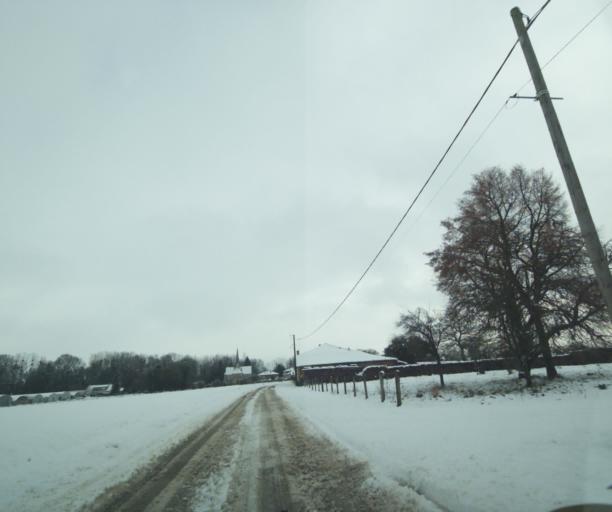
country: FR
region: Champagne-Ardenne
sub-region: Departement de la Haute-Marne
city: Montier-en-Der
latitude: 48.4967
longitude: 4.6973
